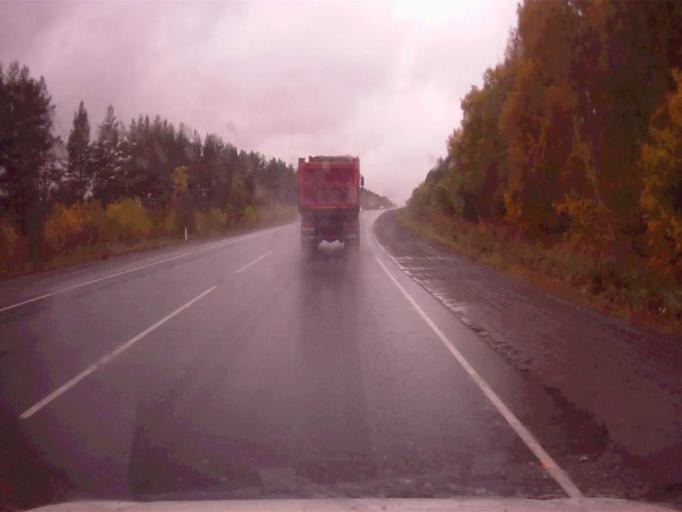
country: RU
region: Chelyabinsk
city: Roshchino
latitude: 55.3576
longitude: 61.2369
